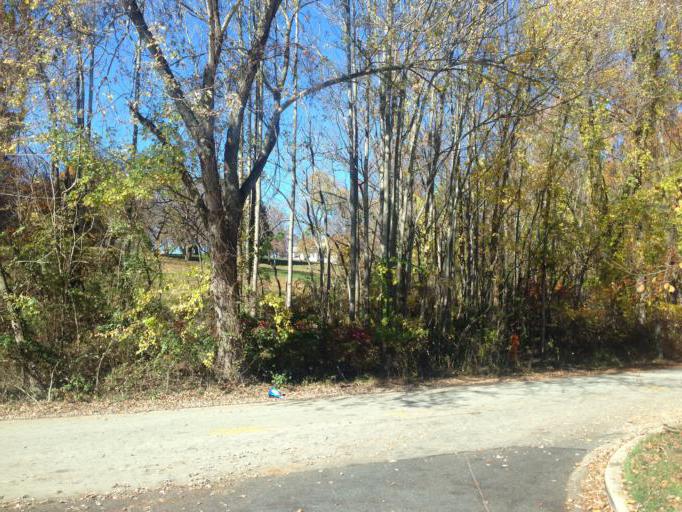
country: US
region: Maryland
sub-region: Howard County
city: Columbia
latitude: 39.2083
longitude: -76.8590
